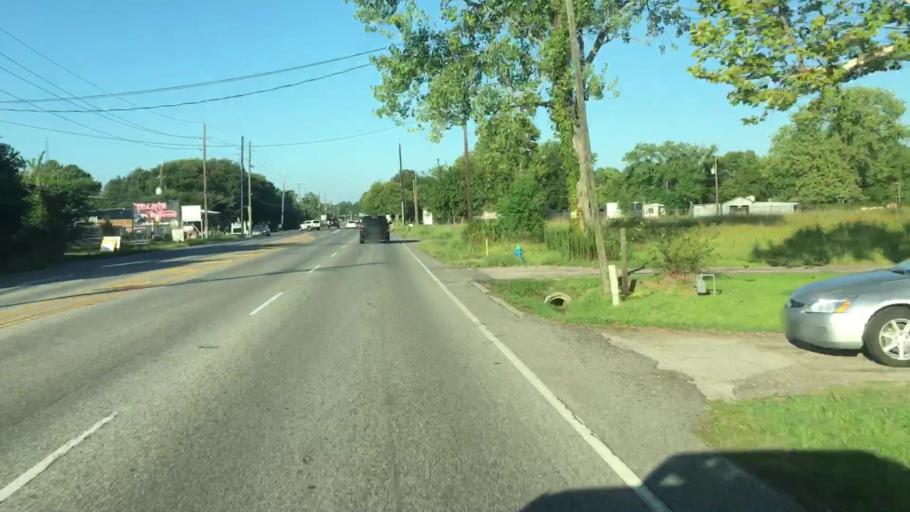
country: US
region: Texas
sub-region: Harris County
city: Humble
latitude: 29.9599
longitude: -95.2579
